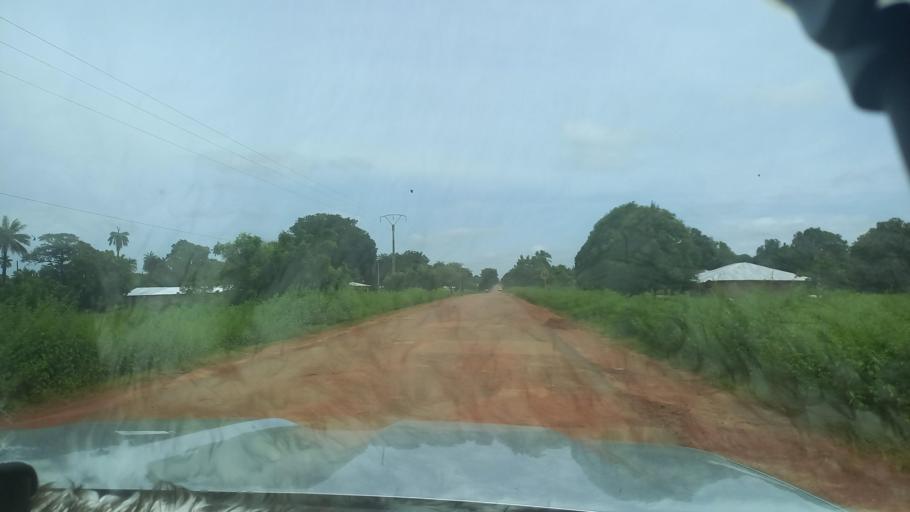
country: SN
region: Kolda
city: Marsassoum
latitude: 12.9665
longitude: -15.9629
